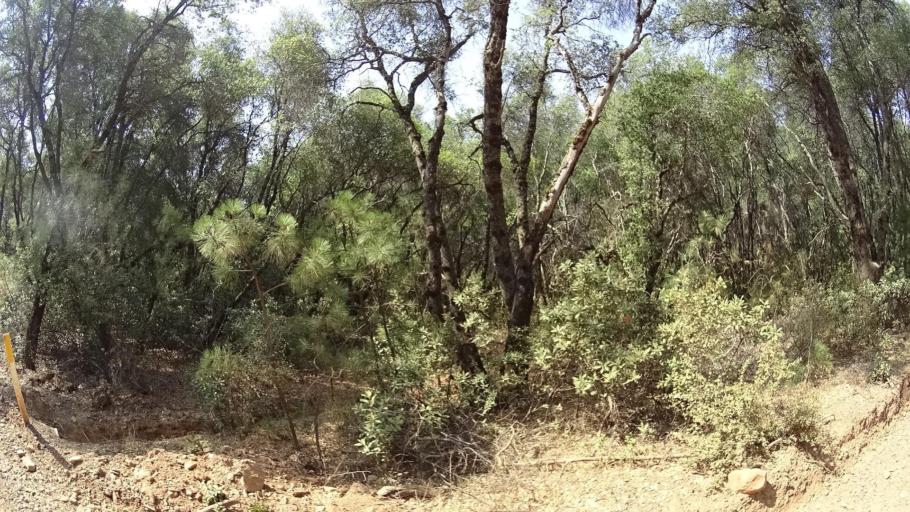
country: US
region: California
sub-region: Mariposa County
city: Midpines
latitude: 37.7001
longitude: -120.1254
